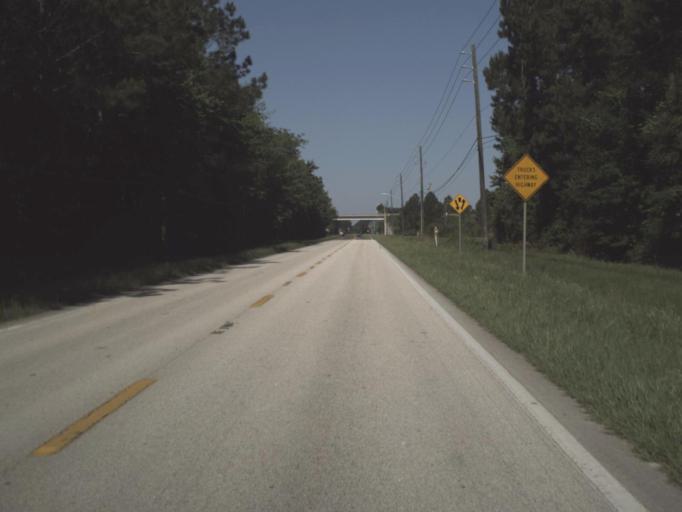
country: US
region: Florida
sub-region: Duval County
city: Baldwin
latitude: 30.3049
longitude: -81.9371
